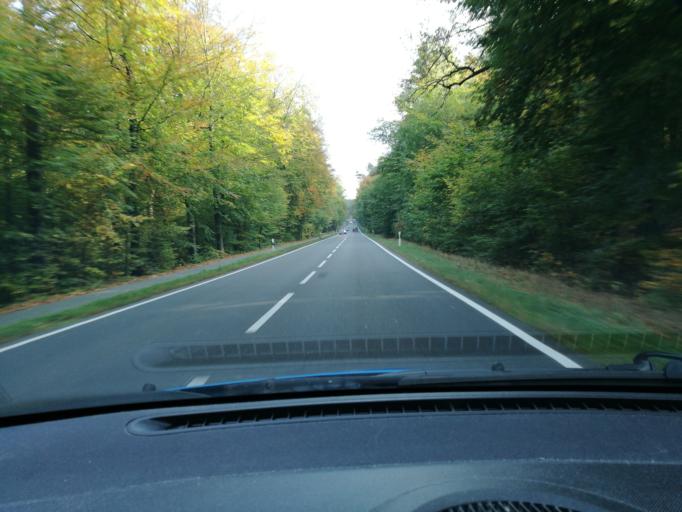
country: DE
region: Lower Saxony
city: Gohrde
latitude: 53.1323
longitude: 10.8959
